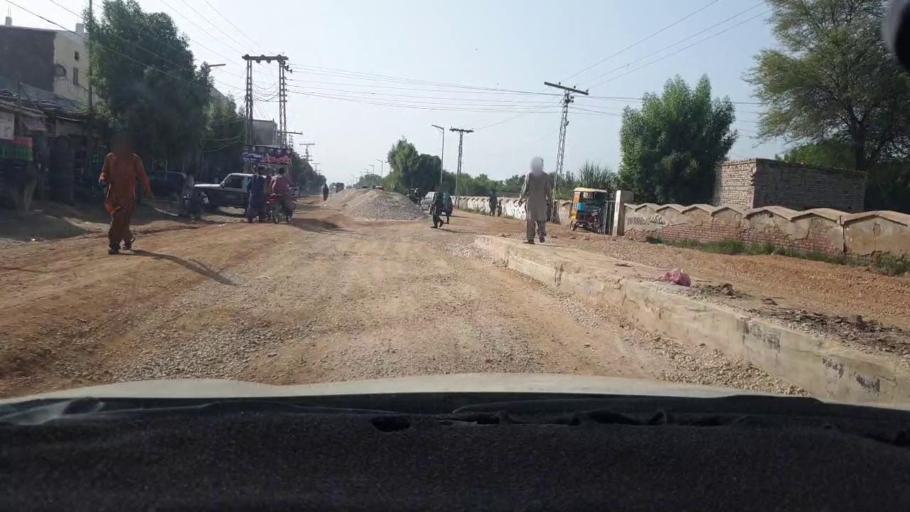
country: PK
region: Sindh
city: Sanghar
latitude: 26.0397
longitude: 68.9503
